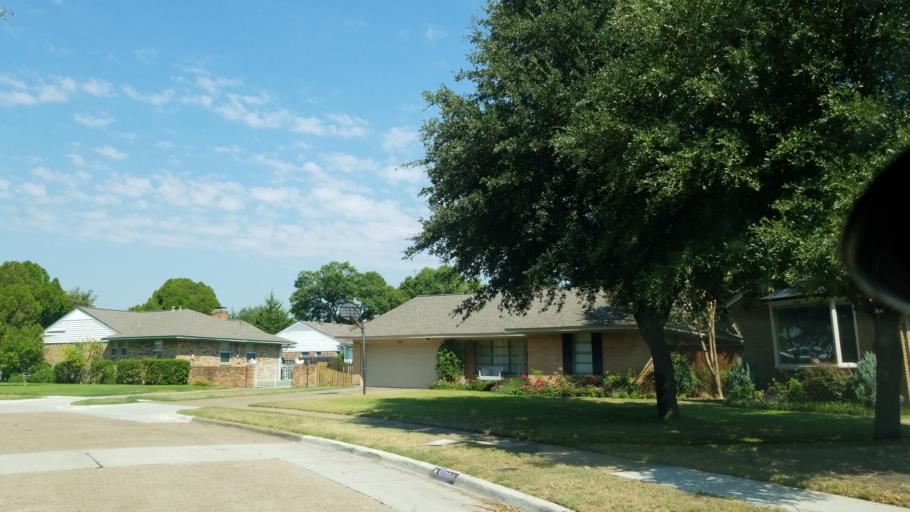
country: US
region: Texas
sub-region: Dallas County
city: Richardson
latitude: 32.8766
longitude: -96.7078
